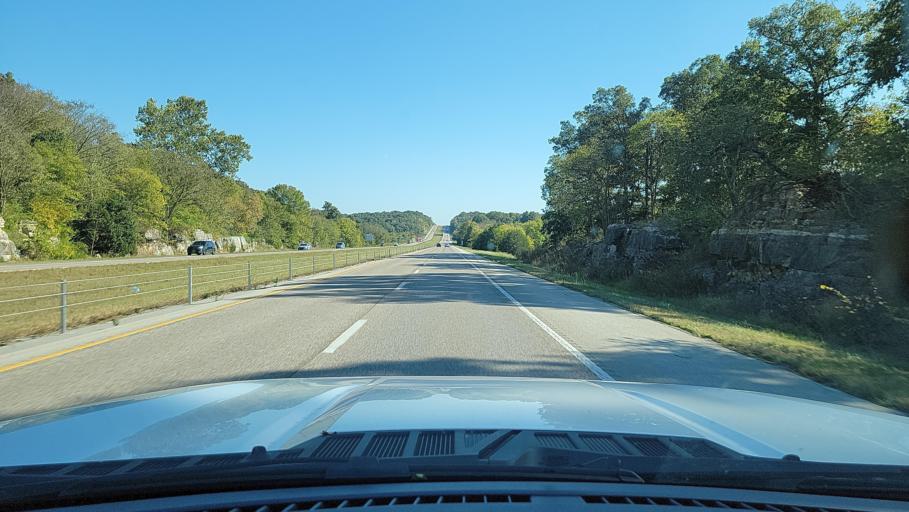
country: US
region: Missouri
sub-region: Sainte Genevieve County
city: Sainte Genevieve
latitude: 37.8641
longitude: -90.0227
